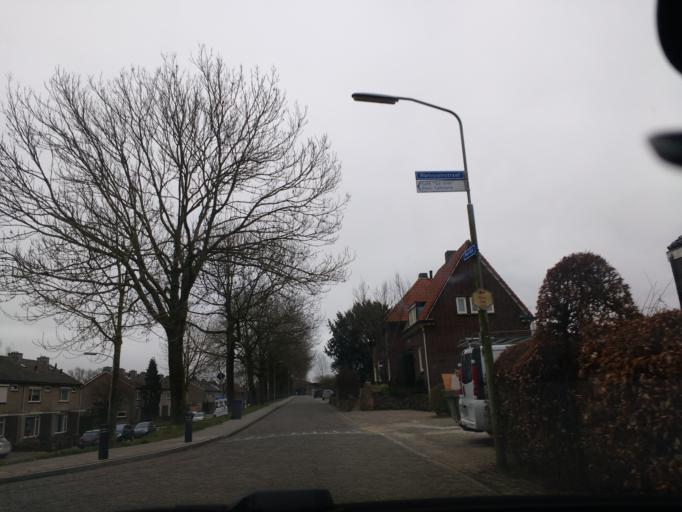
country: NL
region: Gelderland
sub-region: Gemeente Groesbeek
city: Berg en Dal
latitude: 51.8556
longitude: 5.9354
